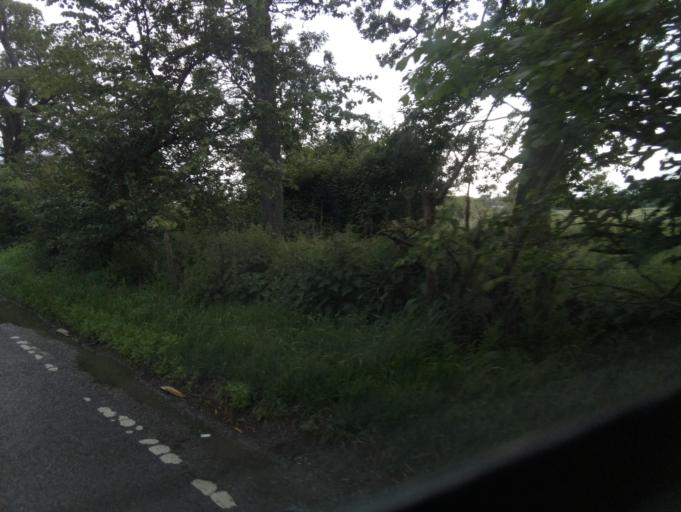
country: GB
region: England
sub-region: Lincolnshire
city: Great Gonerby
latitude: 52.9922
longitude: -0.6708
